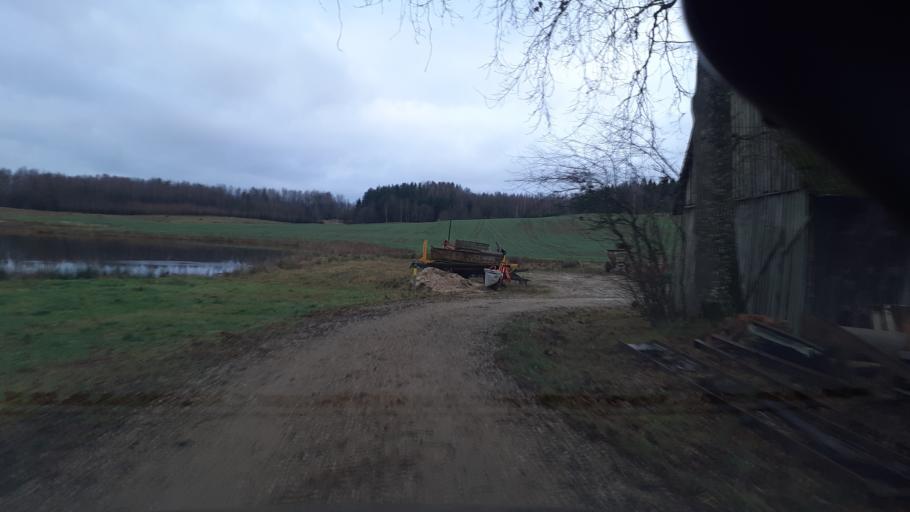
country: LV
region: Alsunga
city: Alsunga
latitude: 56.8794
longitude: 21.6860
